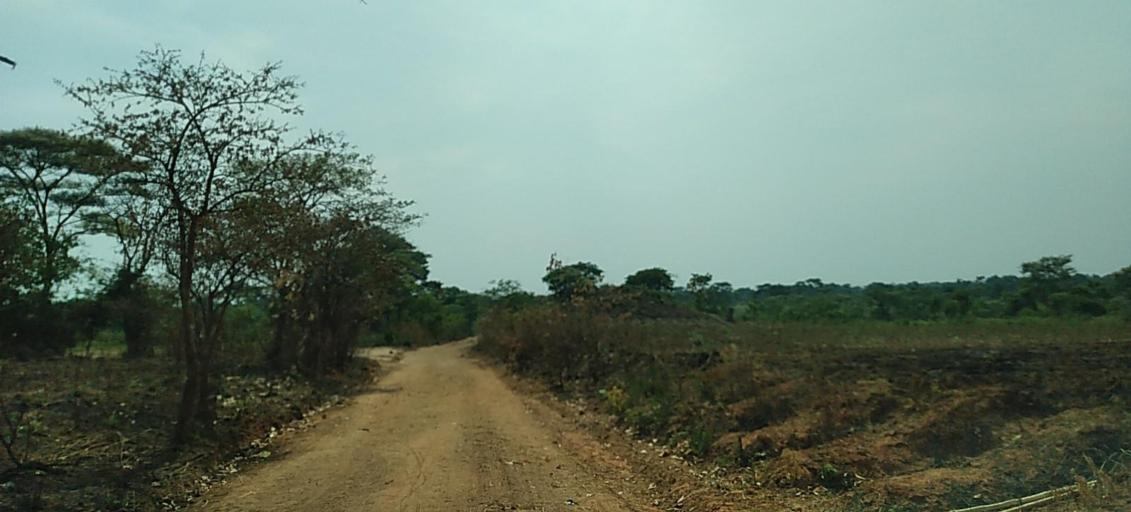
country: ZM
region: Copperbelt
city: Ndola
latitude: -13.2095
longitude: 28.7348
